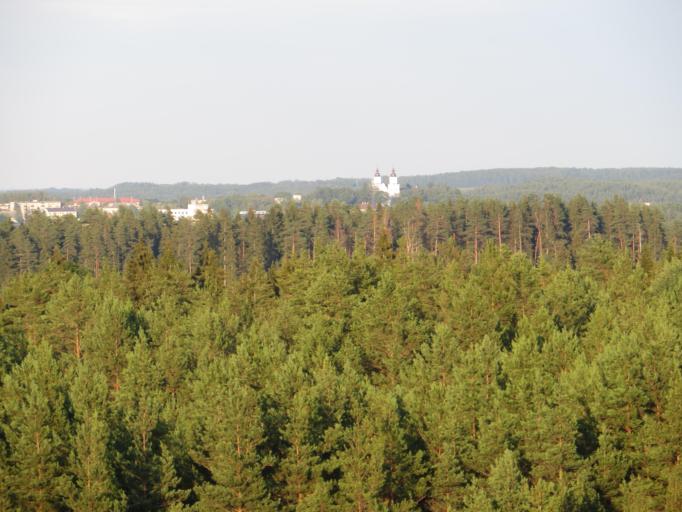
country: LT
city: Zarasai
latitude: 55.7404
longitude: 26.1804
